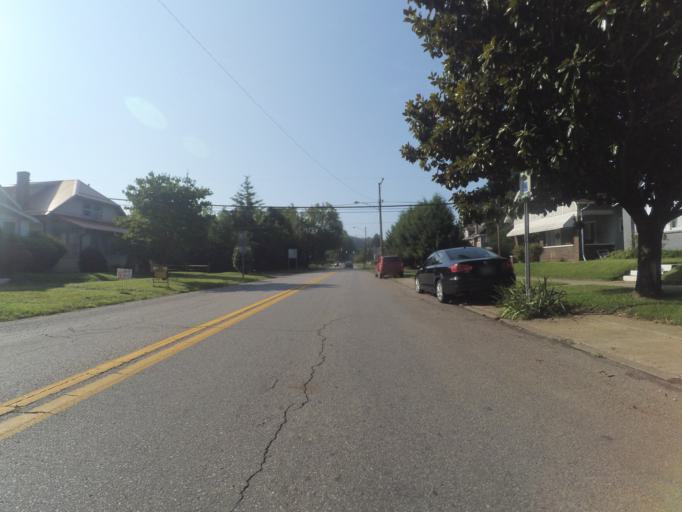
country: US
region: West Virginia
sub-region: Cabell County
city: Huntington
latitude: 38.4134
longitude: -82.4490
